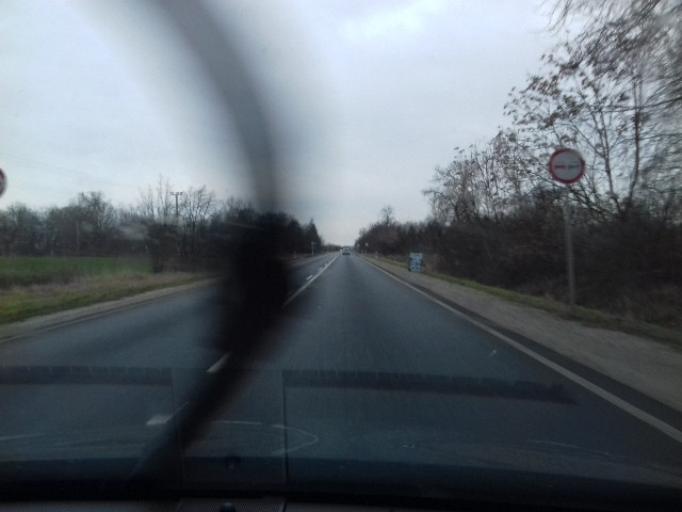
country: HU
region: Szabolcs-Szatmar-Bereg
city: Ujfeherto
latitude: 47.8664
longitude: 21.7050
